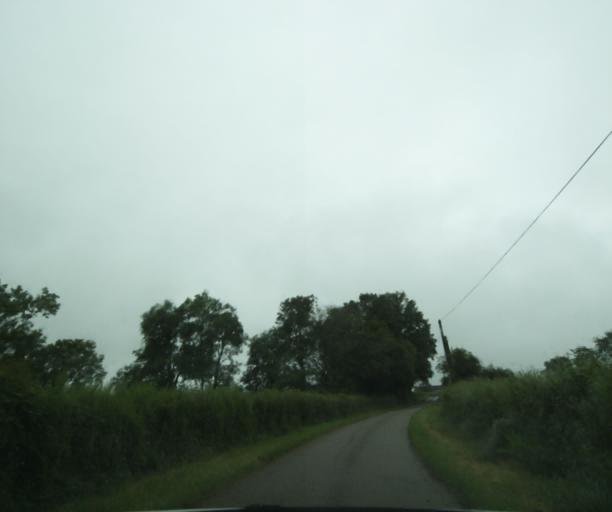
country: FR
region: Bourgogne
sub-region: Departement de Saone-et-Loire
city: Charolles
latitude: 46.4660
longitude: 4.2270
